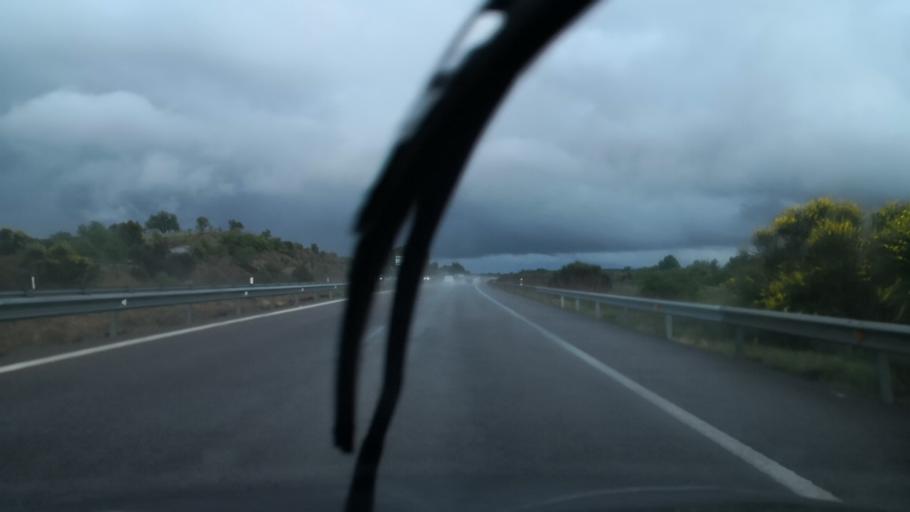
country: ES
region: Extremadura
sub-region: Provincia de Badajoz
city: Valdelacalzada
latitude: 38.8473
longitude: -6.6800
